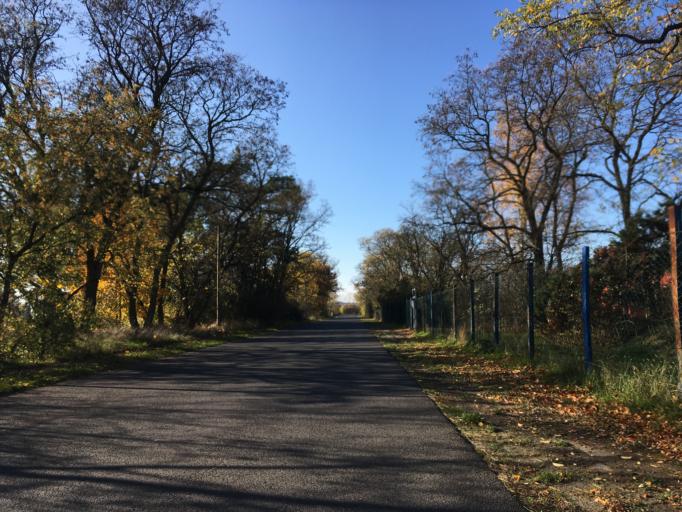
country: DE
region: Brandenburg
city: Spreenhagen
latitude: 52.3407
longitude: 13.8926
